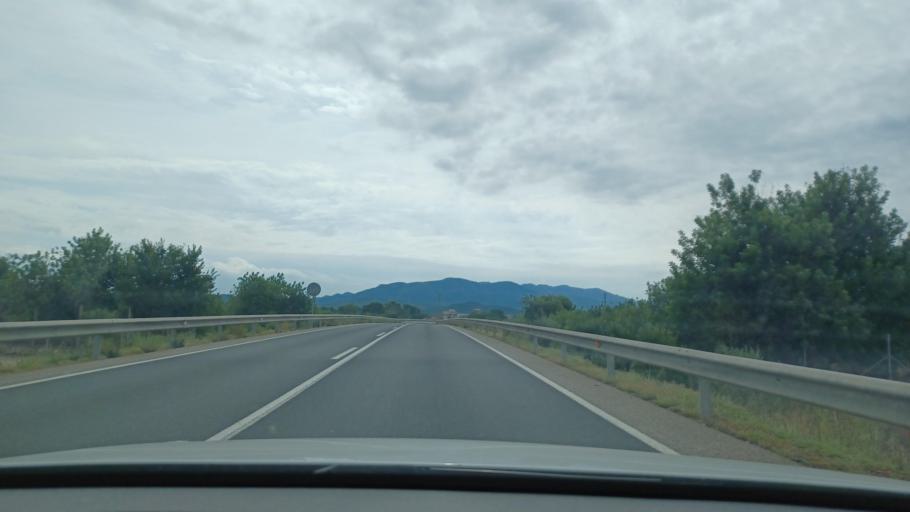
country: ES
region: Catalonia
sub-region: Provincia de Tarragona
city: Santa Barbara
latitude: 40.7219
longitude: 0.5043
